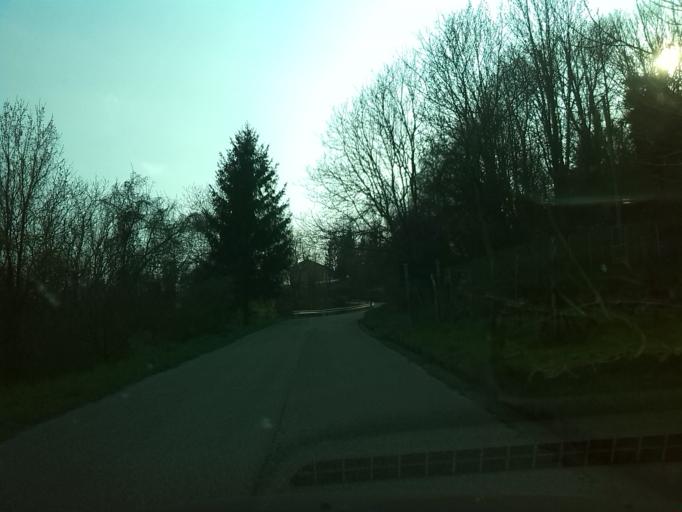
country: IT
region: Friuli Venezia Giulia
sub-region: Provincia di Udine
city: Clodig
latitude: 46.1796
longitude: 13.5733
